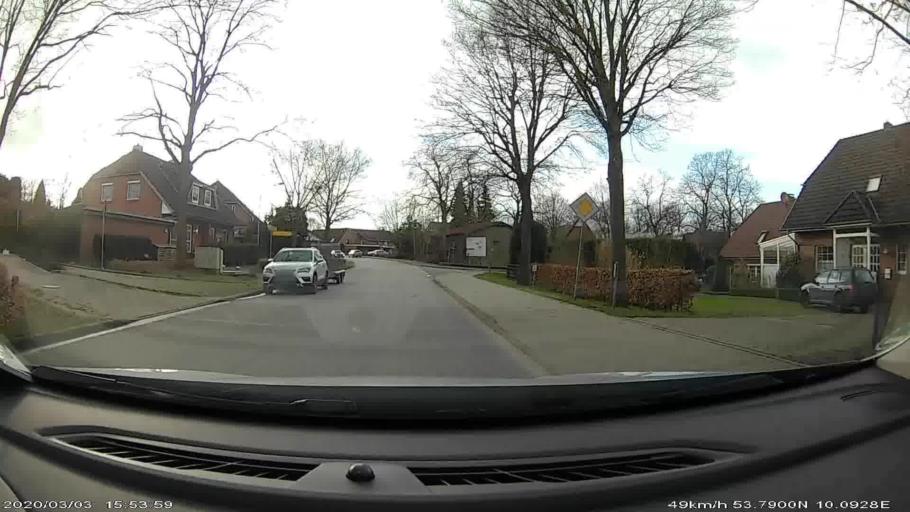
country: DE
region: Schleswig-Holstein
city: Nahe
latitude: 53.7899
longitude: 10.0940
